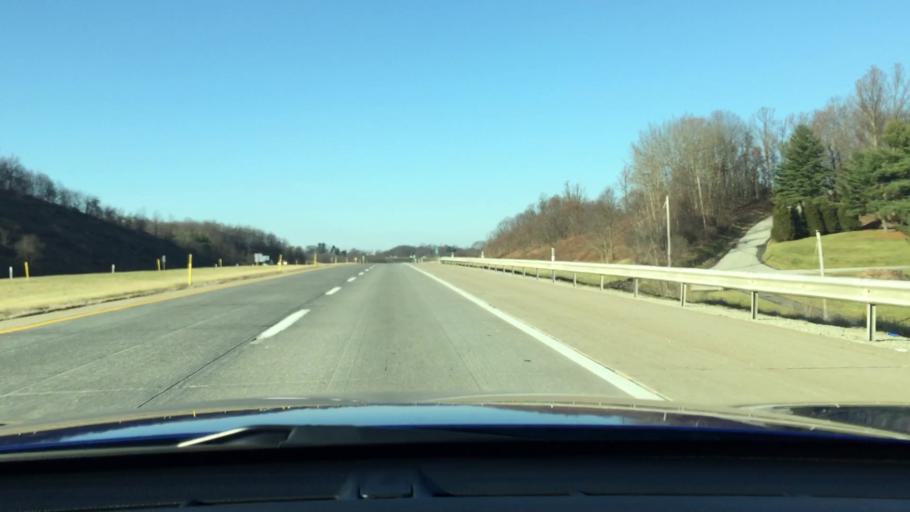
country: US
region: Pennsylvania
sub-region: Westmoreland County
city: New Stanton
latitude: 40.2484
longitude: -79.6097
